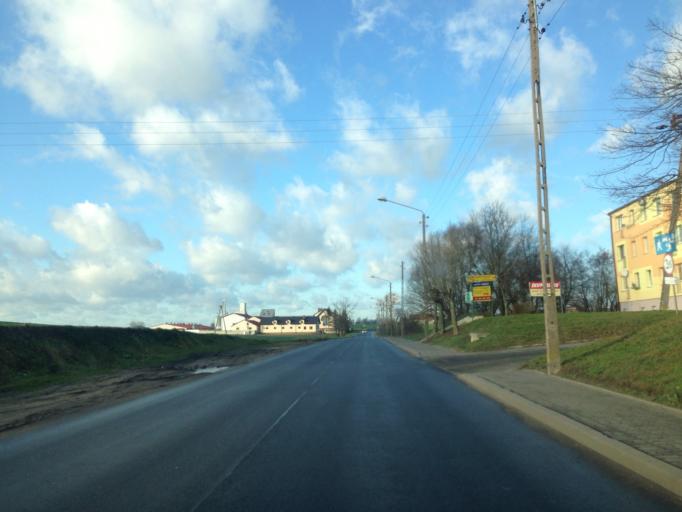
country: PL
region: Kujawsko-Pomorskie
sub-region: Powiat grudziadzki
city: Lasin
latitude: 53.5266
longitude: 19.0786
